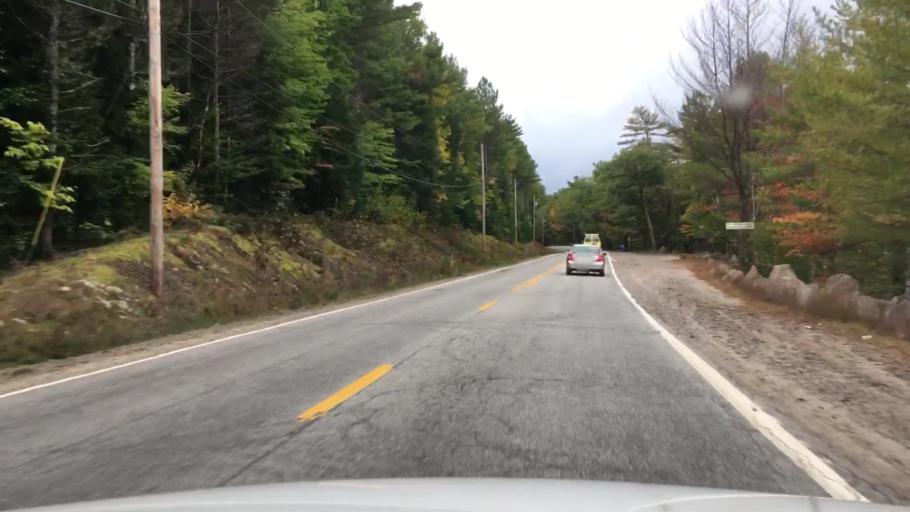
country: US
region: Maine
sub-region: Oxford County
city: Norway
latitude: 44.2221
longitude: -70.6162
